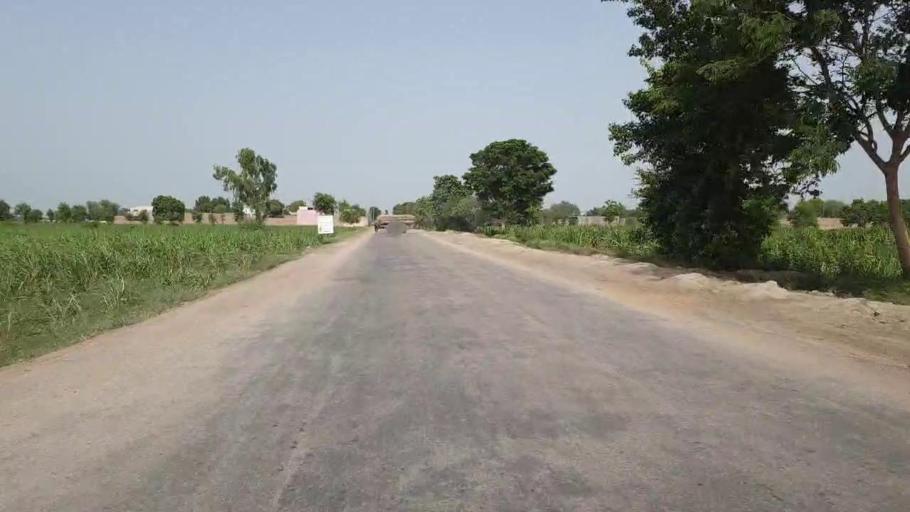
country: PK
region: Sindh
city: Daulatpur
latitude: 26.5605
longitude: 67.9773
